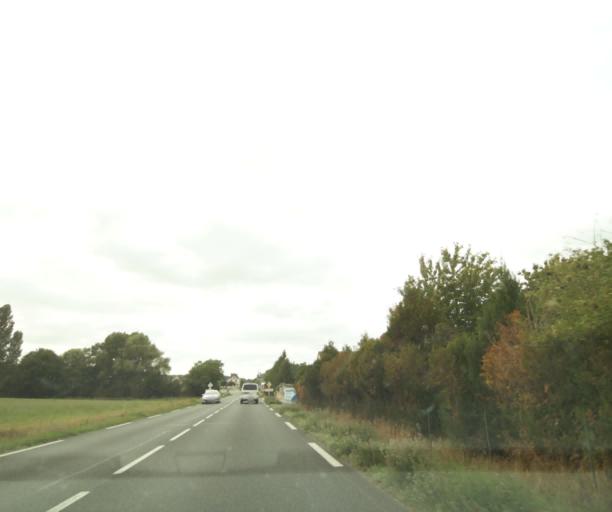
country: FR
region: Centre
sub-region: Departement d'Indre-et-Loire
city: Perrusson
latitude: 47.0819
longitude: 1.0385
